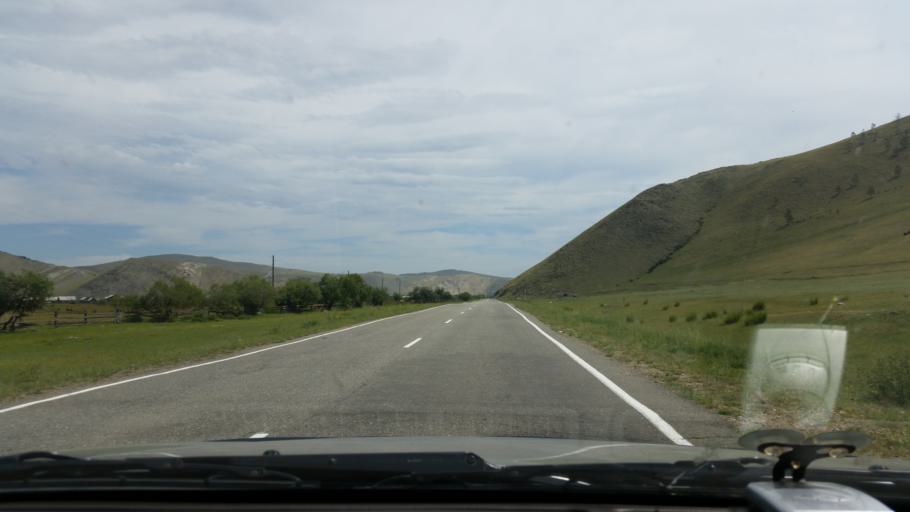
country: RU
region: Irkutsk
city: Yelantsy
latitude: 52.8062
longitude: 106.4548
